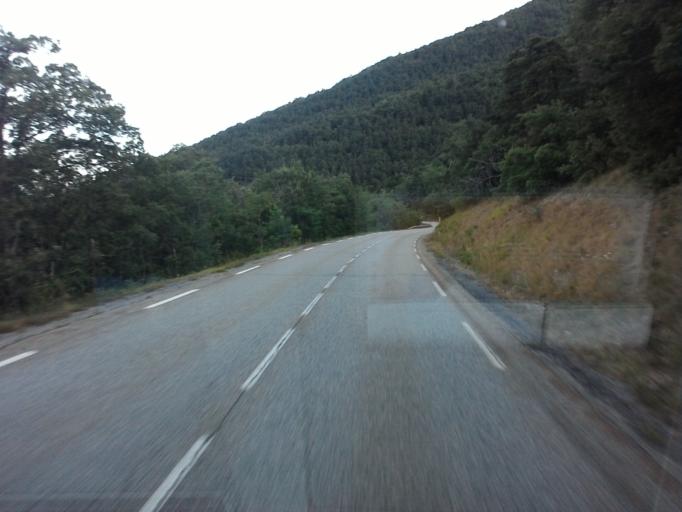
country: FR
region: Rhone-Alpes
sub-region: Departement de l'Isere
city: La Mure
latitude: 44.8344
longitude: 5.8878
